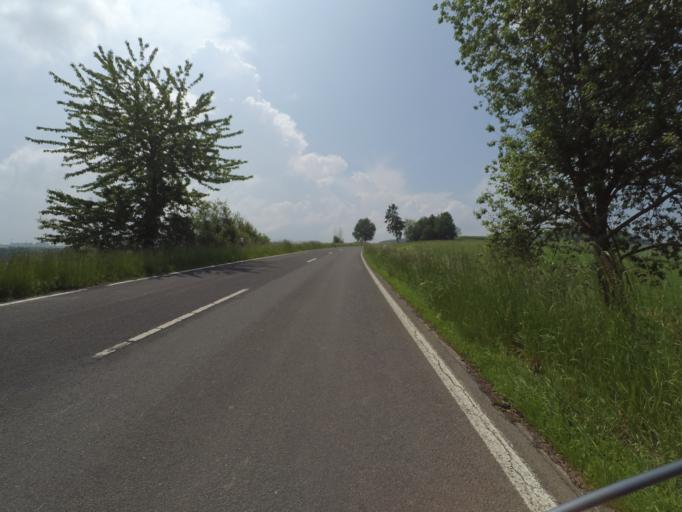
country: DE
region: Rheinland-Pfalz
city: Sosberg
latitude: 50.0716
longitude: 7.3325
